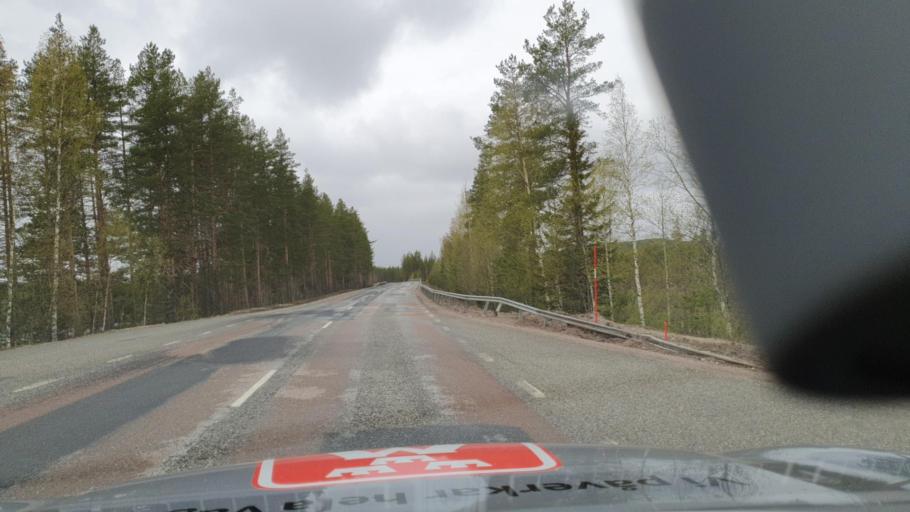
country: SE
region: Vaesternorrland
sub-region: Solleftea Kommun
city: Solleftea
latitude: 63.6501
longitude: 17.3634
